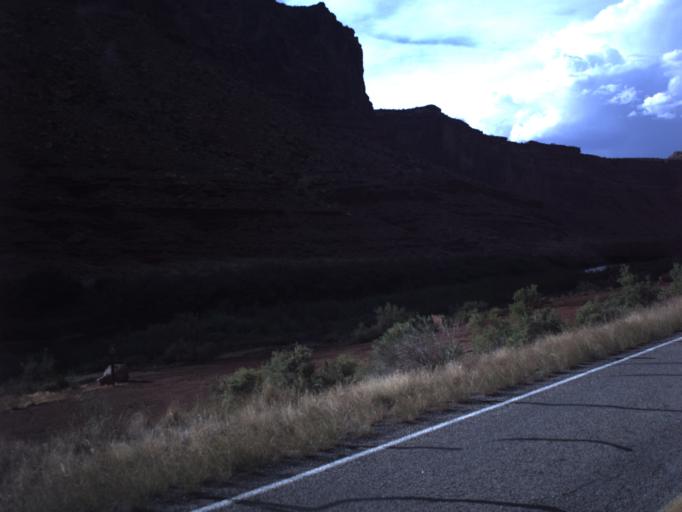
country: US
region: Utah
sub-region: Grand County
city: Moab
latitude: 38.7831
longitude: -109.3324
